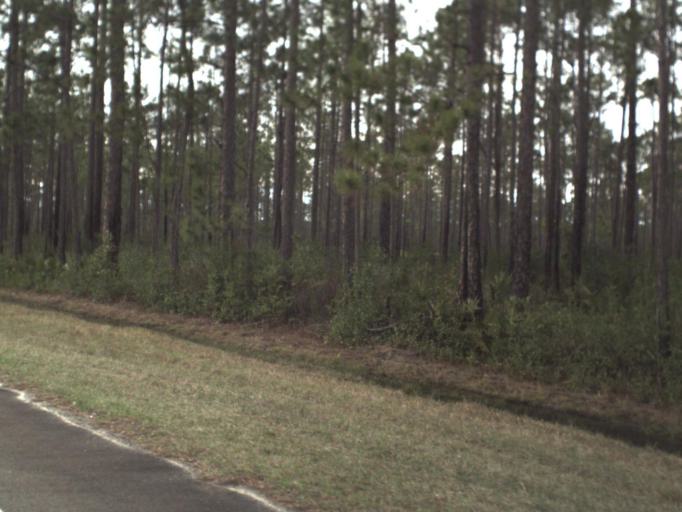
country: US
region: Florida
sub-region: Gulf County
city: Wewahitchka
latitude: 30.1457
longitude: -85.3127
